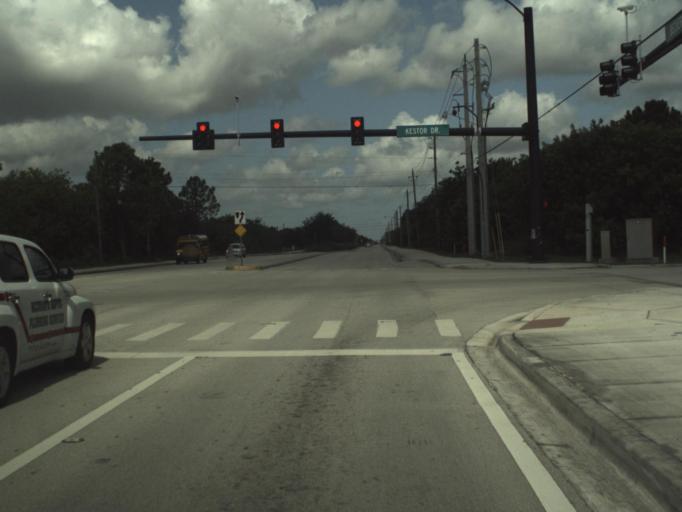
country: US
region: Florida
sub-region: Martin County
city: North River Shores
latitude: 27.2095
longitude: -80.3409
